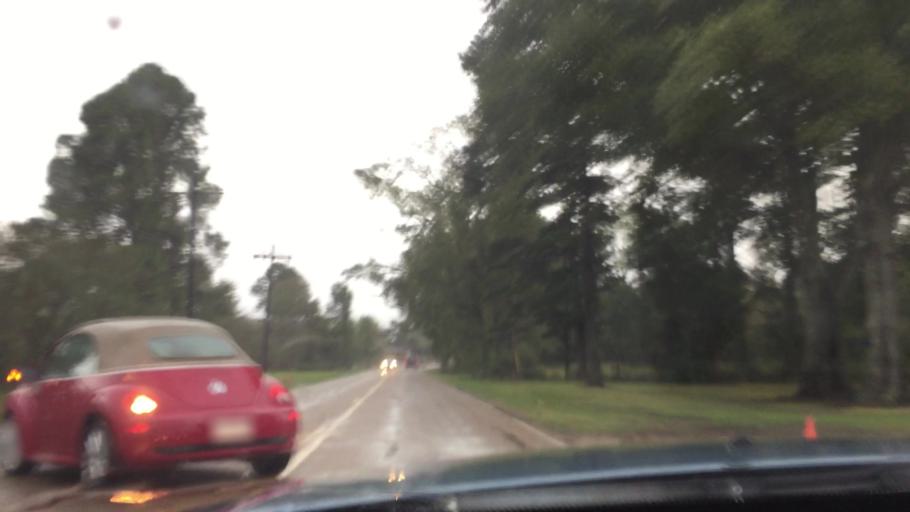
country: US
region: Louisiana
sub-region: East Baton Rouge Parish
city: Monticello
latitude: 30.4482
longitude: -91.0306
